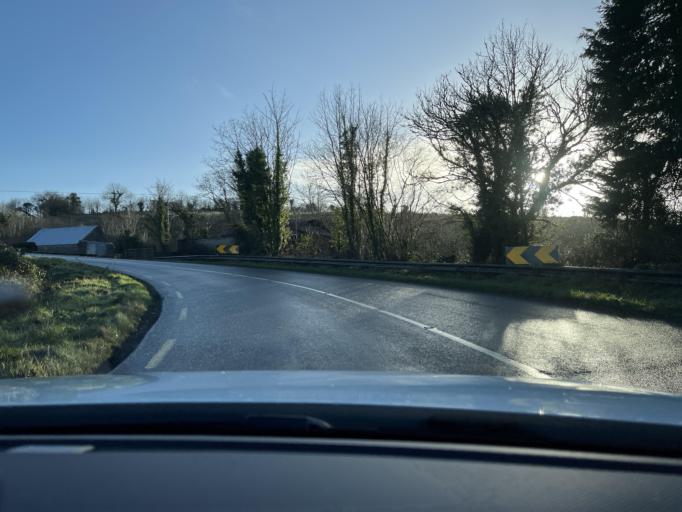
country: IE
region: Connaught
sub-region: County Leitrim
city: Manorhamilton
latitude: 54.2416
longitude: -8.2233
